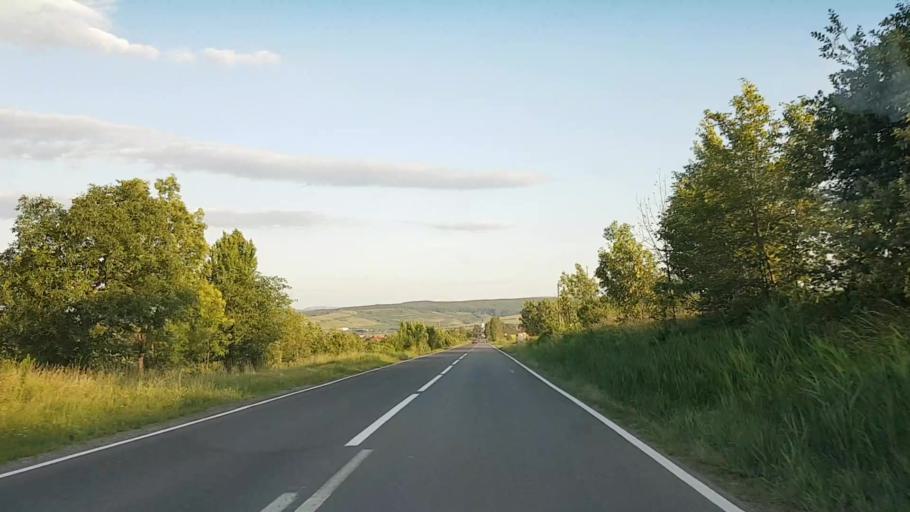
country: RO
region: Harghita
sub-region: Comuna Lupeni
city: Lupeni
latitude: 46.3931
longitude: 25.2143
